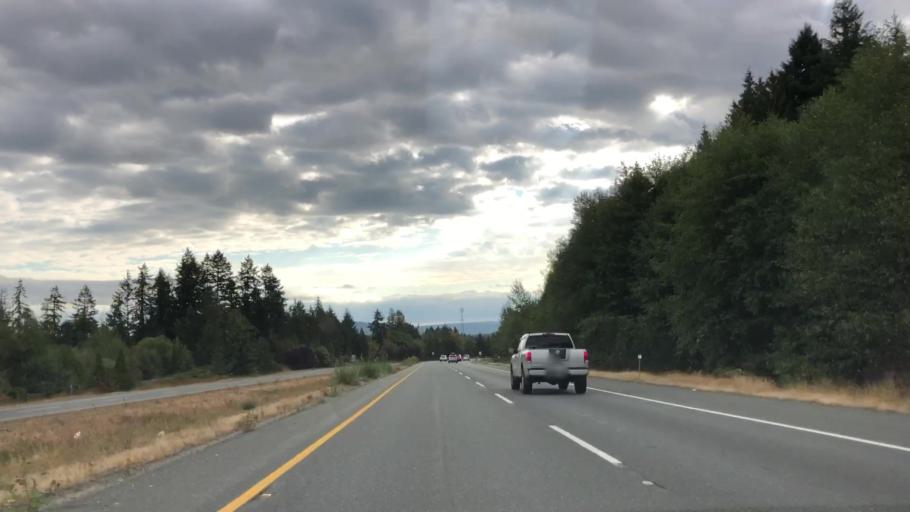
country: CA
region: British Columbia
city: Nanaimo
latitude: 49.1345
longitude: -123.9443
